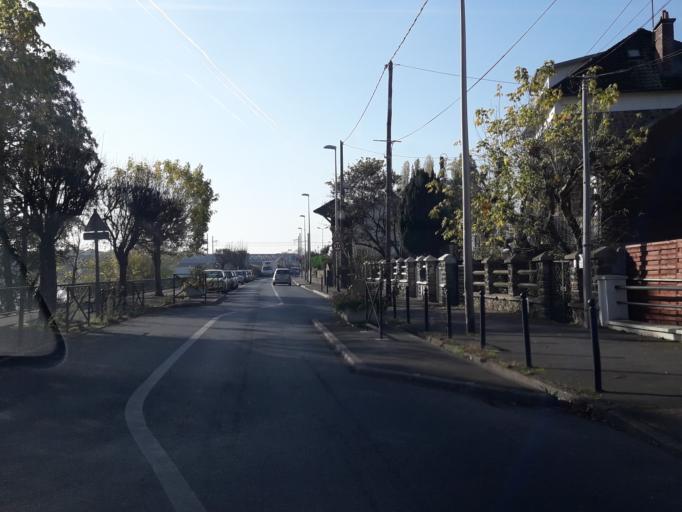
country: FR
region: Ile-de-France
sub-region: Departement de l'Essonne
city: Athis-Mons
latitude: 48.7072
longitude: 2.4019
